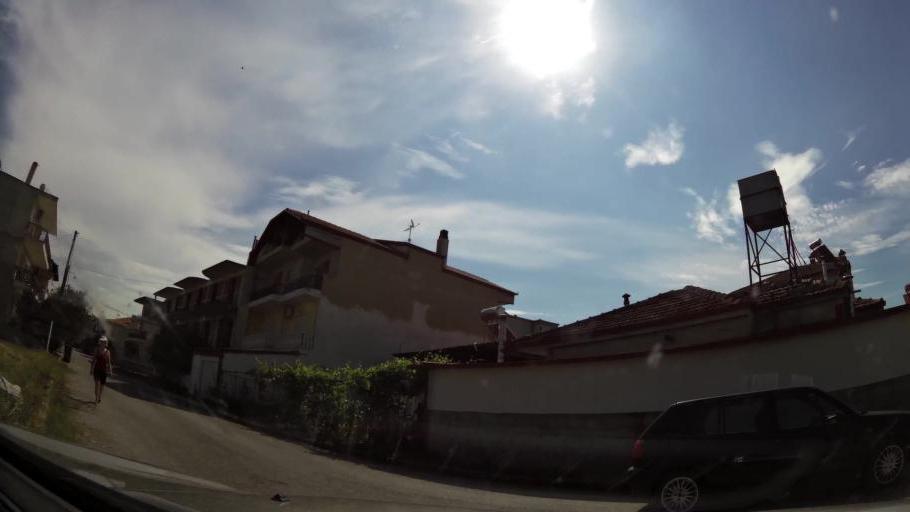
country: GR
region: Central Macedonia
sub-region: Nomos Pierias
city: Katerini
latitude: 40.2736
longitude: 22.4859
